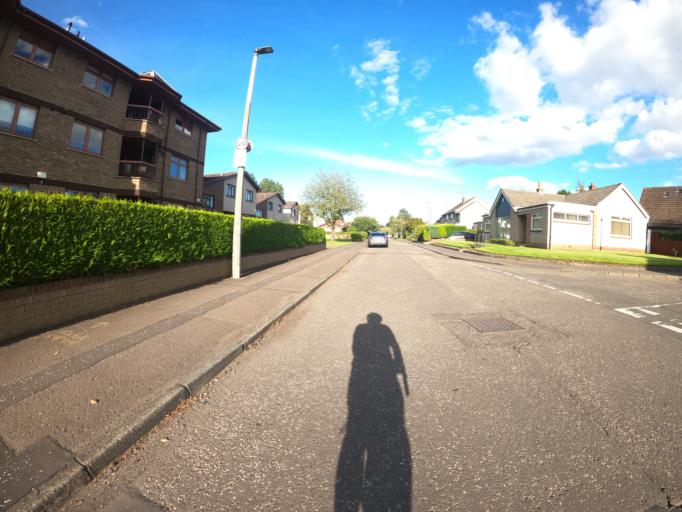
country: GB
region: Scotland
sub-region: Edinburgh
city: Currie
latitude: 55.9620
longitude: -3.3003
